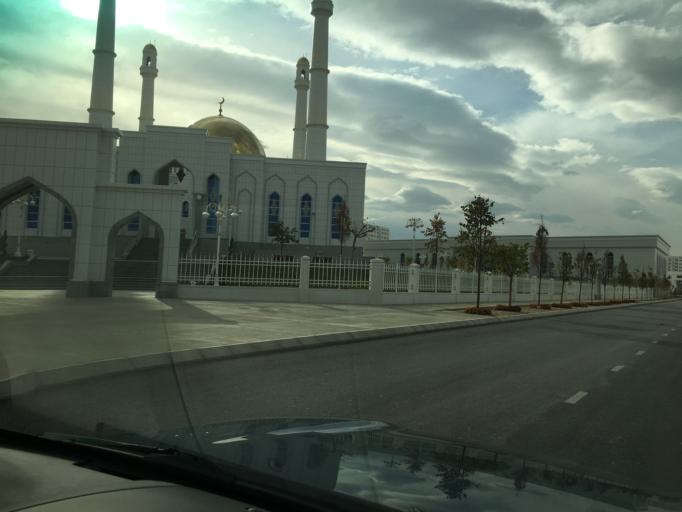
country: TM
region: Ahal
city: Ashgabat
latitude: 37.8986
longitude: 58.4136
